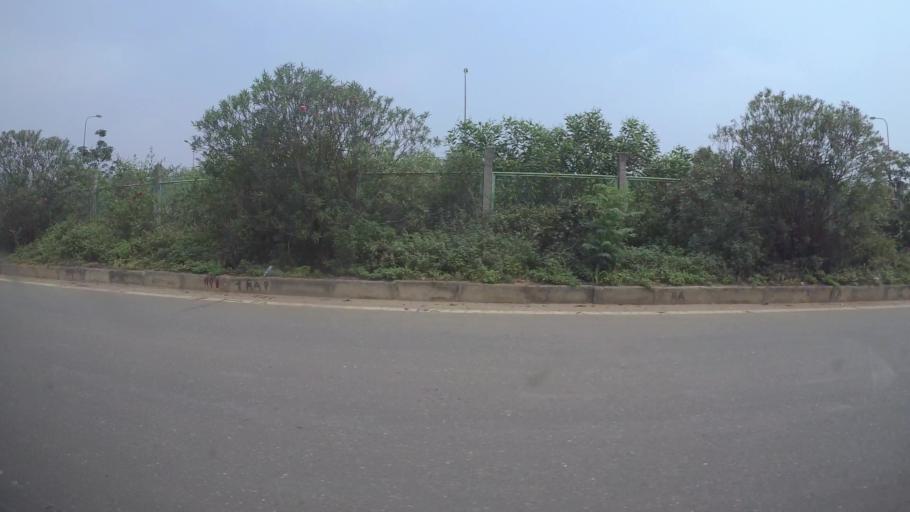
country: VN
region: Ha Noi
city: Quoc Oai
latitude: 20.9885
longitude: 105.5742
